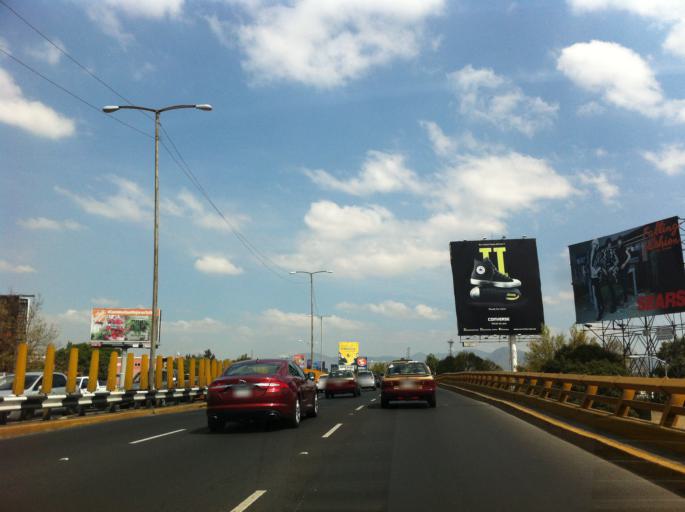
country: MX
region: Mexico City
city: Cuauhtemoc
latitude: 19.4491
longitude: -99.1644
